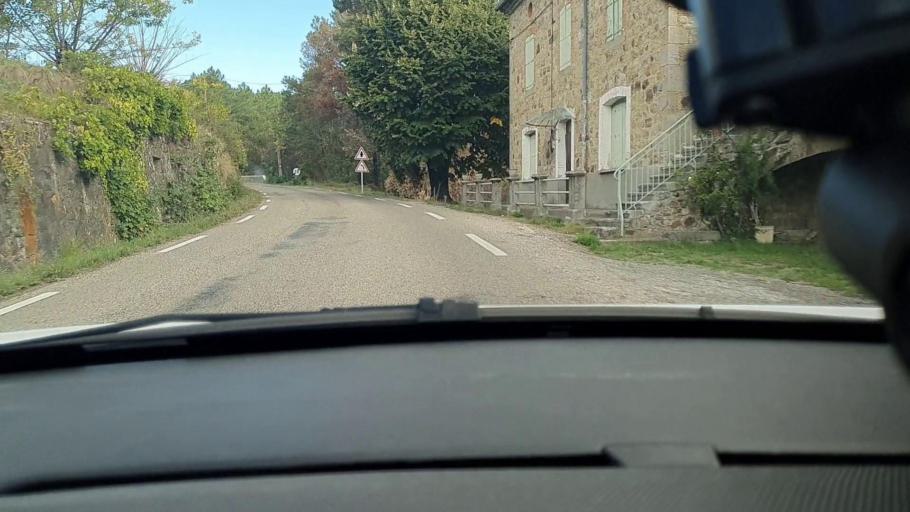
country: FR
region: Languedoc-Roussillon
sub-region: Departement du Gard
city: Besseges
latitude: 44.3146
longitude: 4.0869
